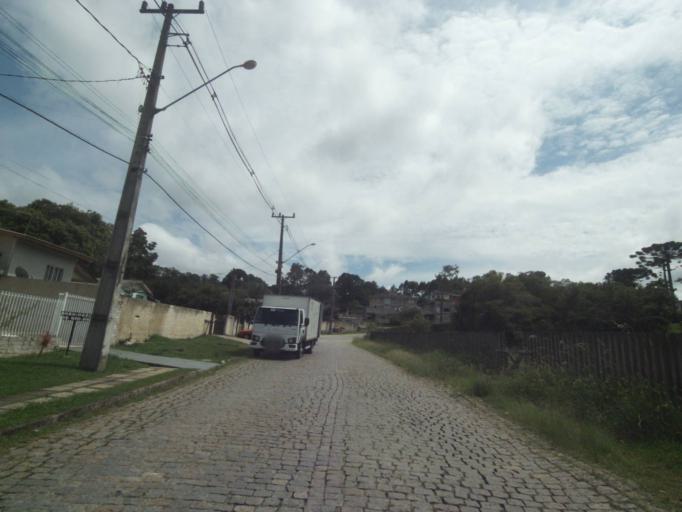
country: BR
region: Parana
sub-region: Campina Grande Do Sul
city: Campina Grande do Sul
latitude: -25.3078
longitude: -49.0476
